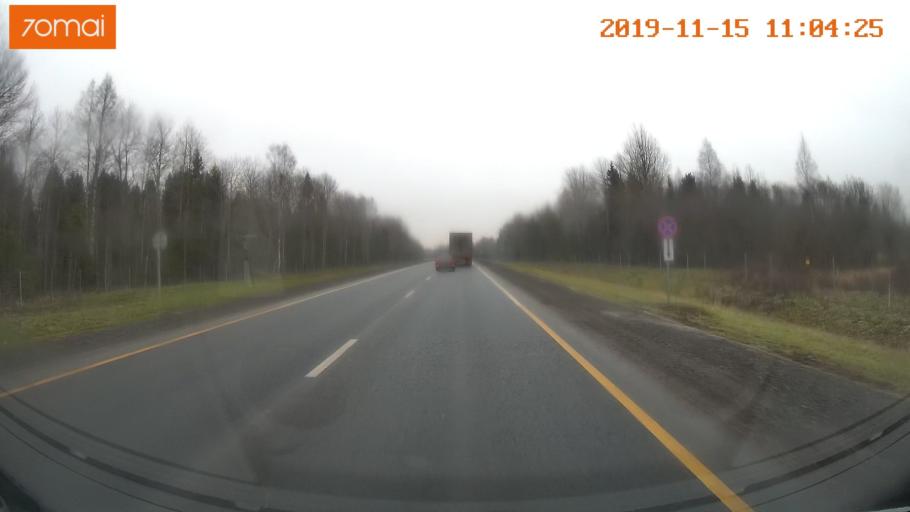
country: RU
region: Vologda
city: Chebsara
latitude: 59.1201
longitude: 38.9838
